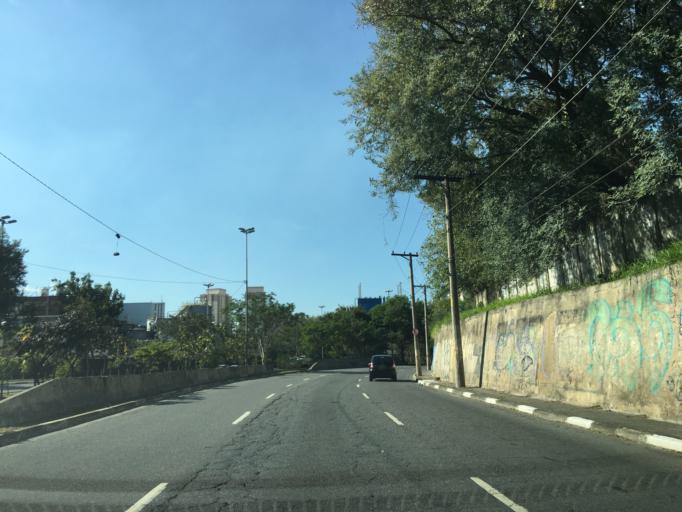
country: BR
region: Sao Paulo
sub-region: Osasco
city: Osasco
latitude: -23.5577
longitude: -46.7425
